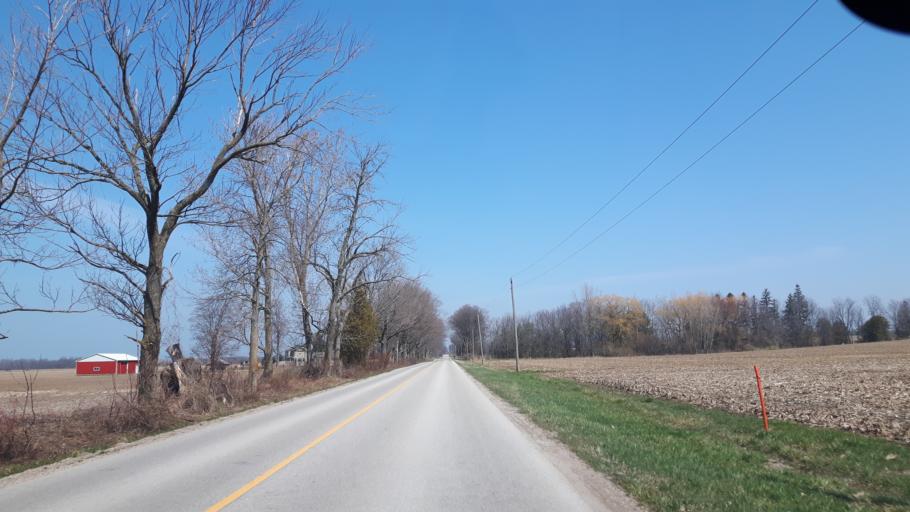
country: CA
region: Ontario
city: Goderich
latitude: 43.6905
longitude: -81.6847
